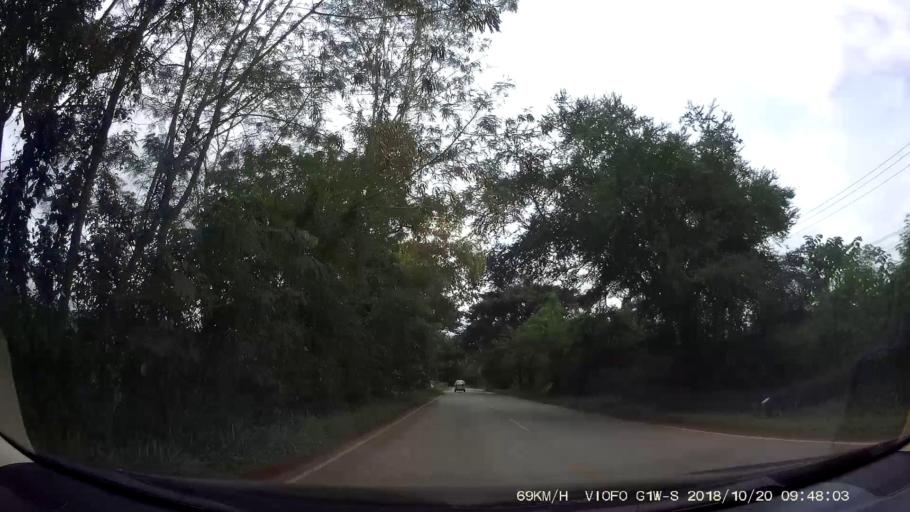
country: TH
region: Chaiyaphum
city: Khon San
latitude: 16.5083
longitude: 101.9150
